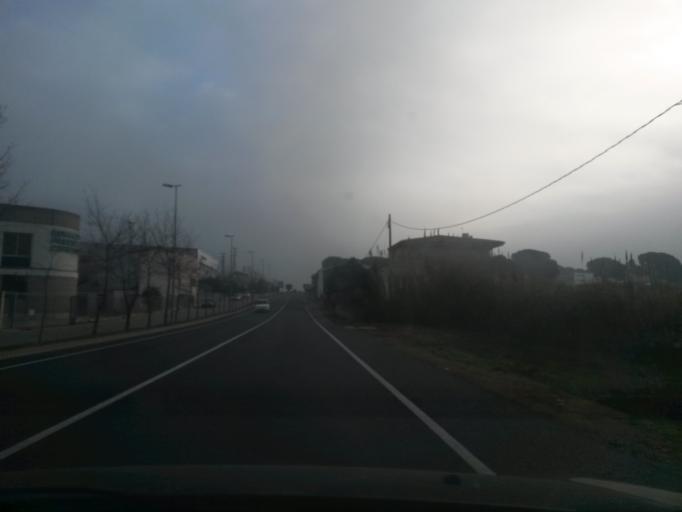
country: ES
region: Catalonia
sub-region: Provincia de Girona
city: Llagostera
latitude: 41.8292
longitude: 2.9035
